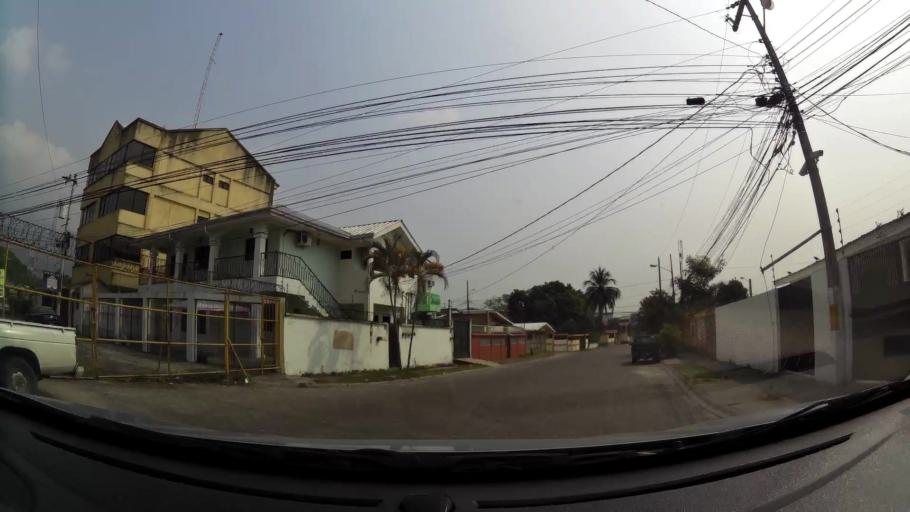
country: HN
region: Cortes
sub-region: San Pedro Sula
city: Pena Blanca
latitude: 15.5275
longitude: -88.0311
